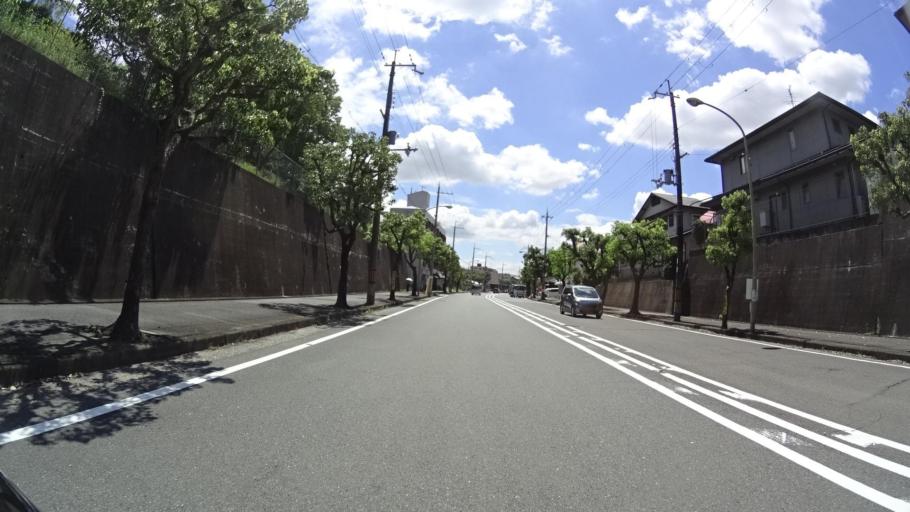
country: JP
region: Kyoto
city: Yawata
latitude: 34.8704
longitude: 135.6907
